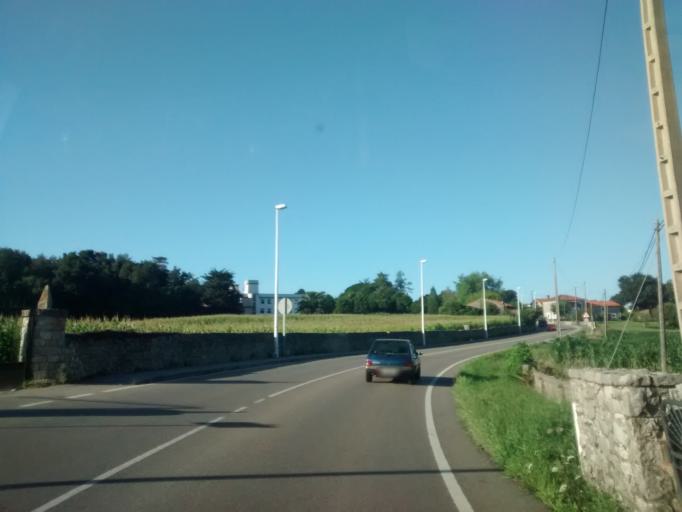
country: ES
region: Cantabria
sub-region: Provincia de Cantabria
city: Santander
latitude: 43.4327
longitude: -3.7729
